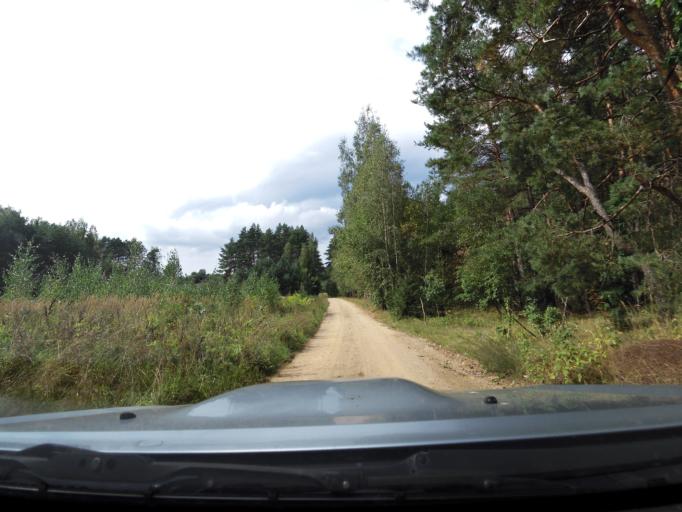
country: LT
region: Vilnius County
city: Elektrenai
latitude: 54.9194
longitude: 24.7470
